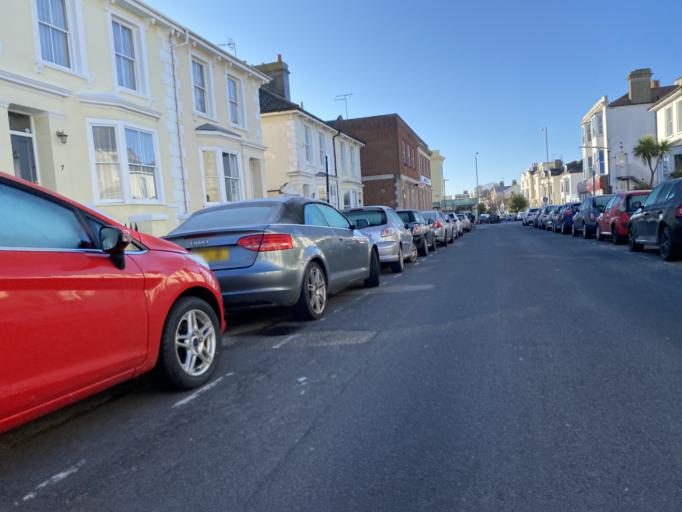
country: GB
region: England
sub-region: Brighton and Hove
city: Hove
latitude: 50.8286
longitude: -0.1721
